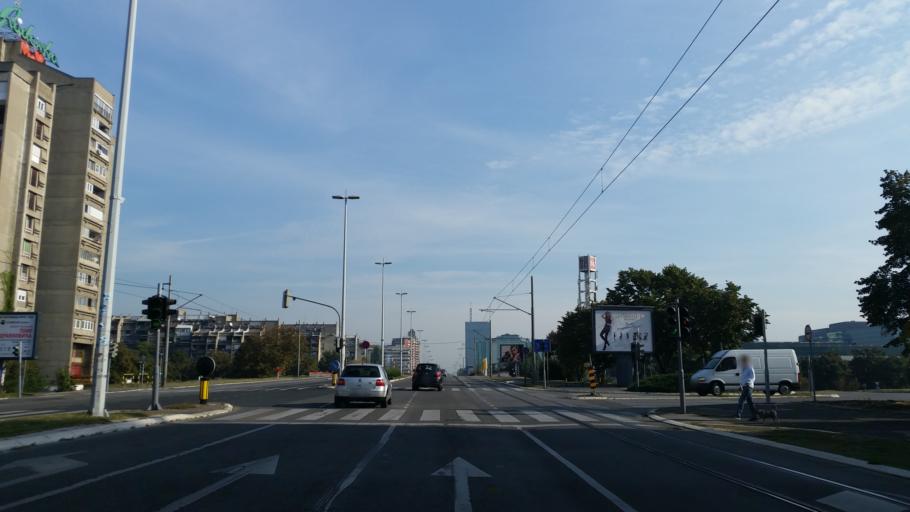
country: RS
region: Central Serbia
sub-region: Belgrade
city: Novi Beograd
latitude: 44.8070
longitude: 20.4278
